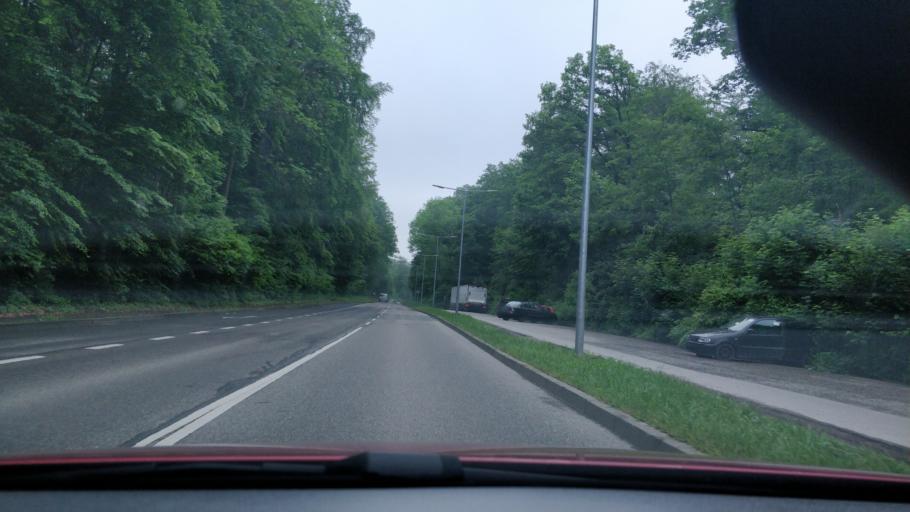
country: DE
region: Baden-Wuerttemberg
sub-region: Regierungsbezirk Stuttgart
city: Leinfelden-Echterdingen
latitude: 48.7263
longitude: 9.1905
